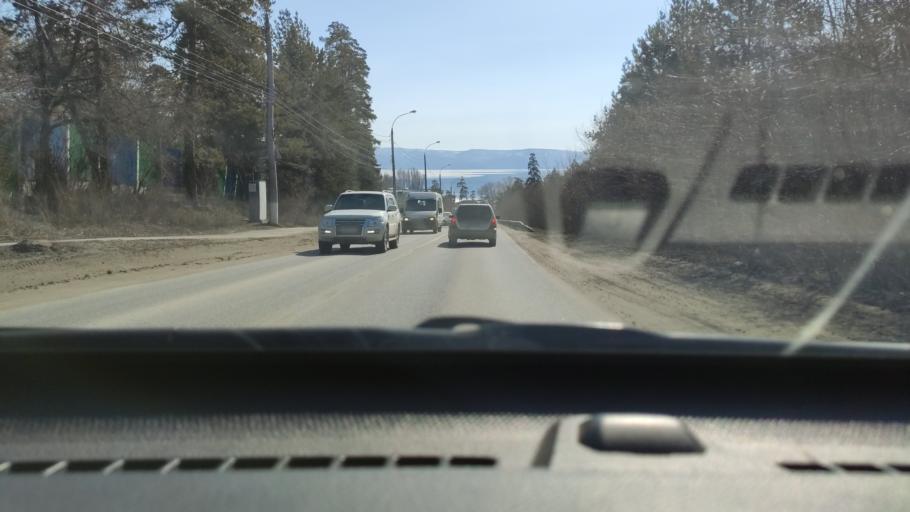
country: RU
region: Samara
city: Tol'yatti
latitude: 53.4843
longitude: 49.3277
